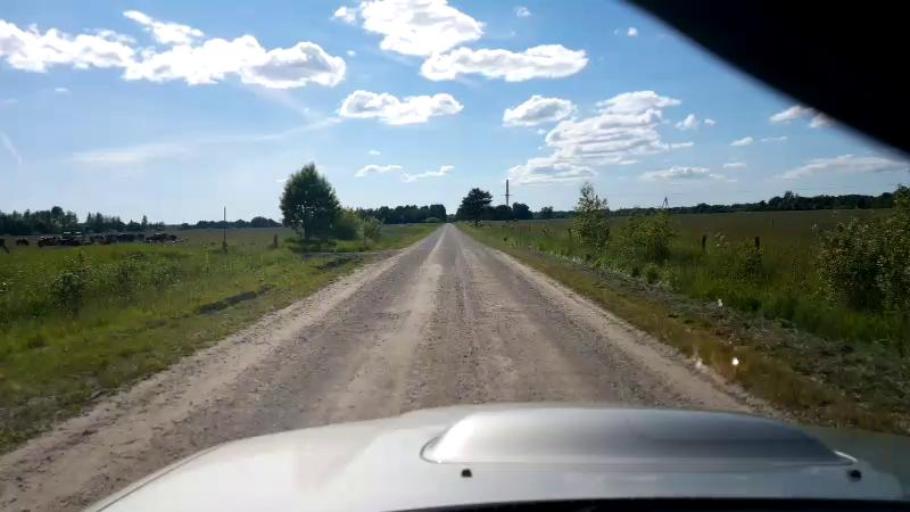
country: EE
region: Paernumaa
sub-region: Sauga vald
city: Sauga
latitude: 58.5091
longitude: 24.5746
